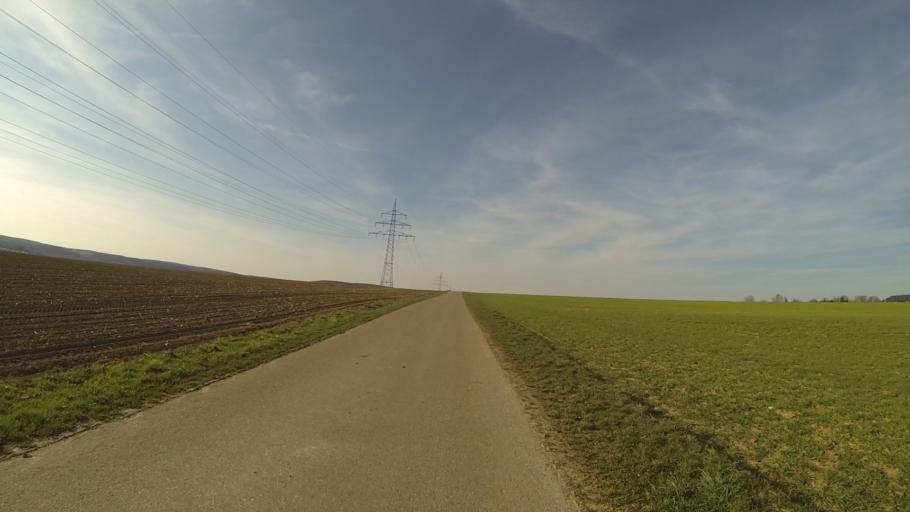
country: DE
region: Baden-Wuerttemberg
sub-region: Regierungsbezirk Stuttgart
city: Herbrechtingen
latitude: 48.6120
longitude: 10.1944
